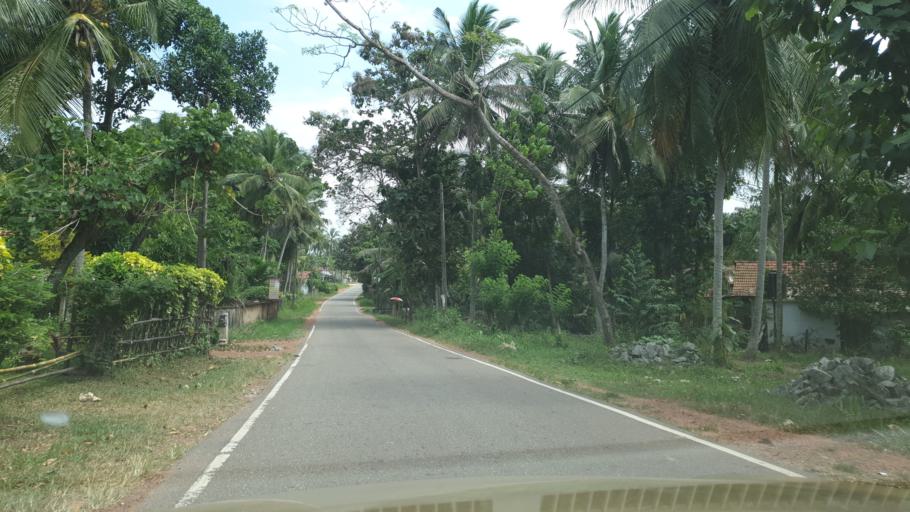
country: LK
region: North Western
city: Kuliyapitiya
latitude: 7.3548
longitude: 79.9740
